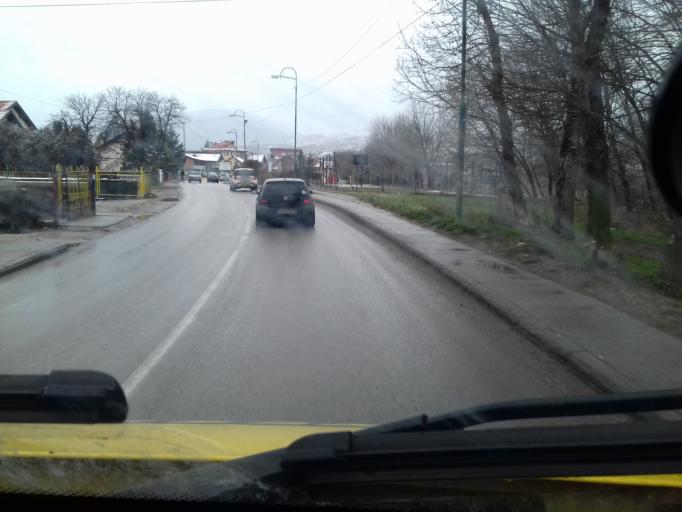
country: BA
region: Federation of Bosnia and Herzegovina
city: Kakanj
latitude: 44.1182
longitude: 18.1158
